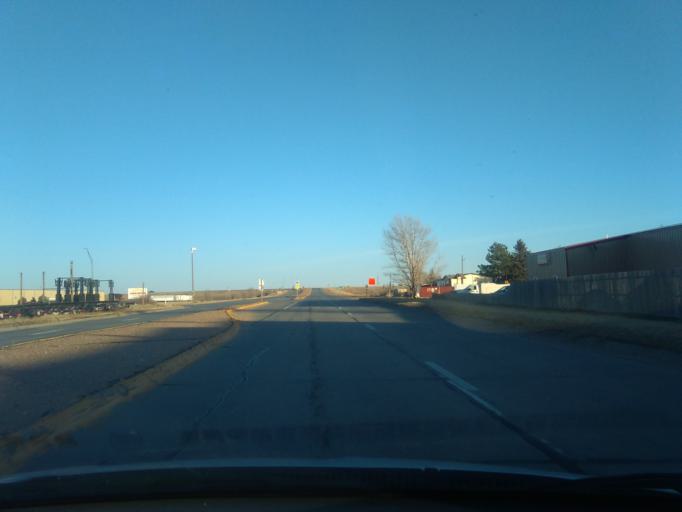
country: US
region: Nebraska
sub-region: Cheyenne County
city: Sidney
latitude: 41.1447
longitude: -102.9531
